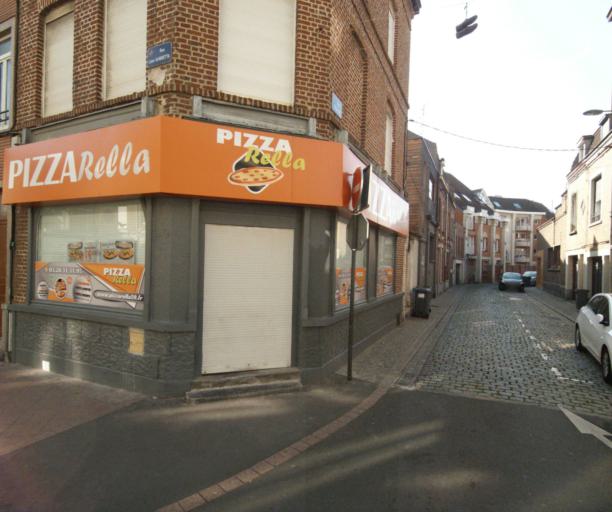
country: FR
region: Nord-Pas-de-Calais
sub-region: Departement du Nord
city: Lille
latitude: 50.6257
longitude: 3.0454
